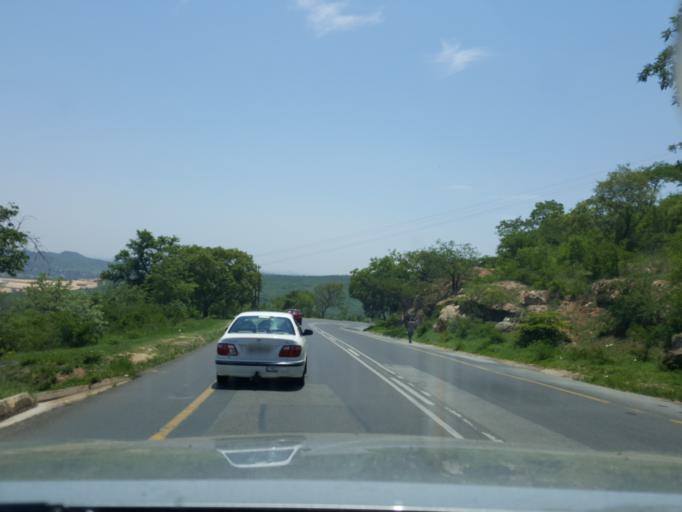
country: ZA
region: Limpopo
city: Thulamahashi
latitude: -24.8317
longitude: 31.0750
